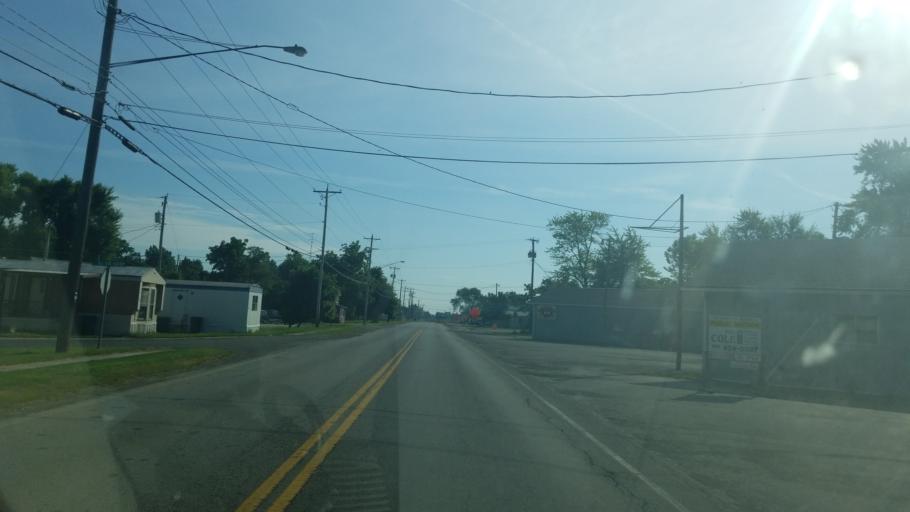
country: US
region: Ohio
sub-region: Hancock County
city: Findlay
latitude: 41.0196
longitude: -83.6728
